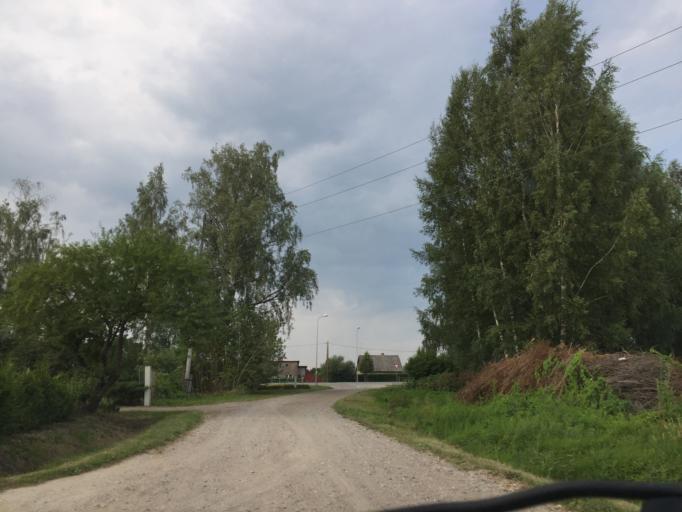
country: LV
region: Jelgava
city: Jelgava
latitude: 56.6520
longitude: 23.6843
